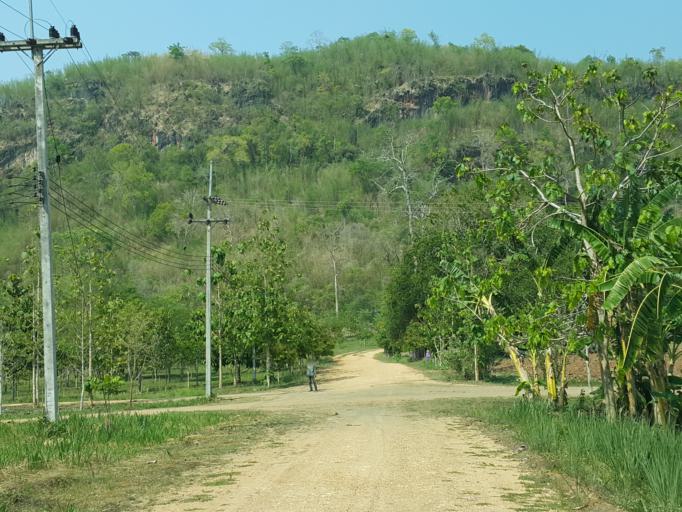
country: TH
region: Kanchanaburi
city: Si Sawat
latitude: 14.4043
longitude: 98.8564
